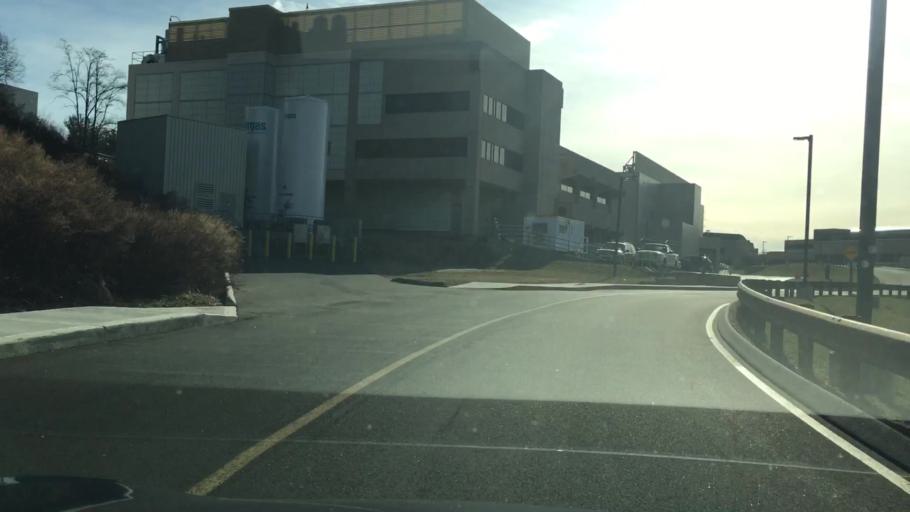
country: US
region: Connecticut
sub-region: Fairfield County
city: Danbury
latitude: 41.3778
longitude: -73.5091
